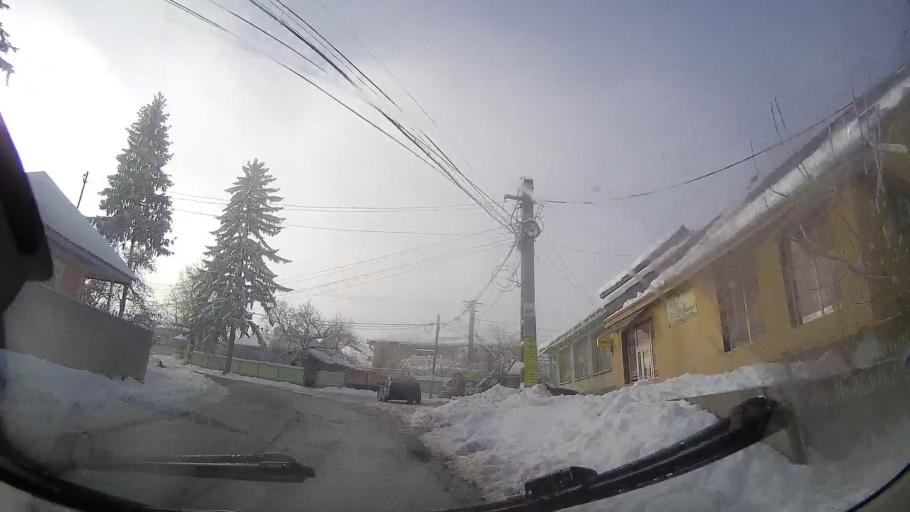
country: RO
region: Iasi
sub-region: Comuna Valea Seaca
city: Topile
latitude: 47.2495
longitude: 26.6600
